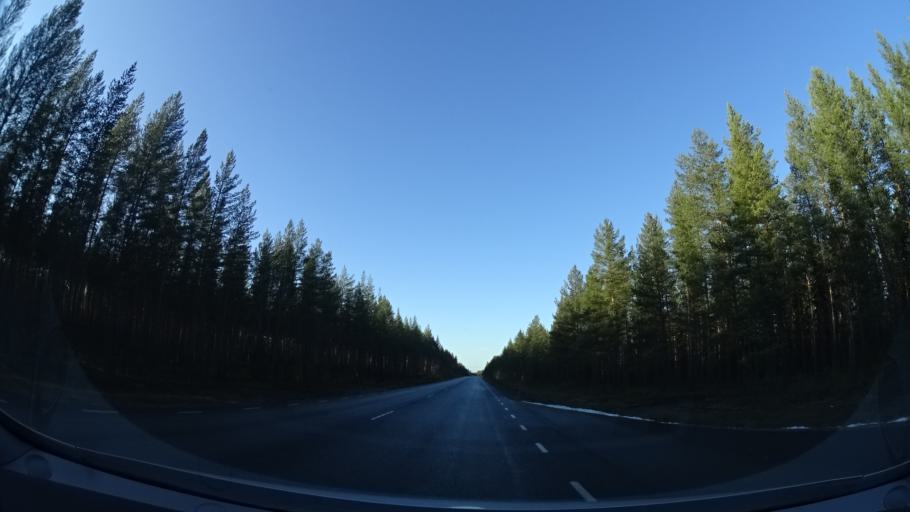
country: SE
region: Vaesterbotten
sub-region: Skelleftea Kommun
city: Langsele
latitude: 64.9379
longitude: 19.9419
